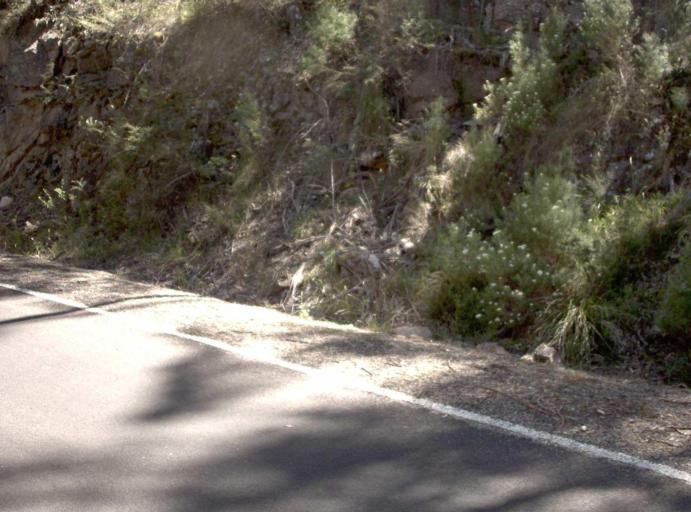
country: AU
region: Victoria
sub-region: East Gippsland
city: Lakes Entrance
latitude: -37.3799
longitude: 148.2191
